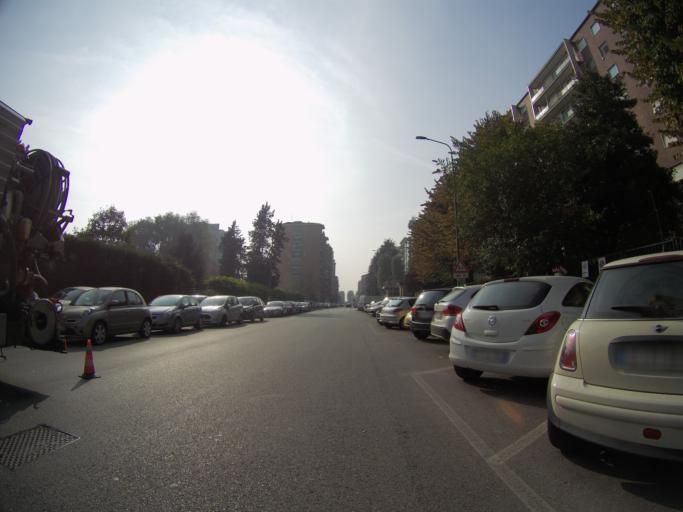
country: IT
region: Lombardy
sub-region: Citta metropolitana di Milano
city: Linate
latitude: 45.4734
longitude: 9.2366
